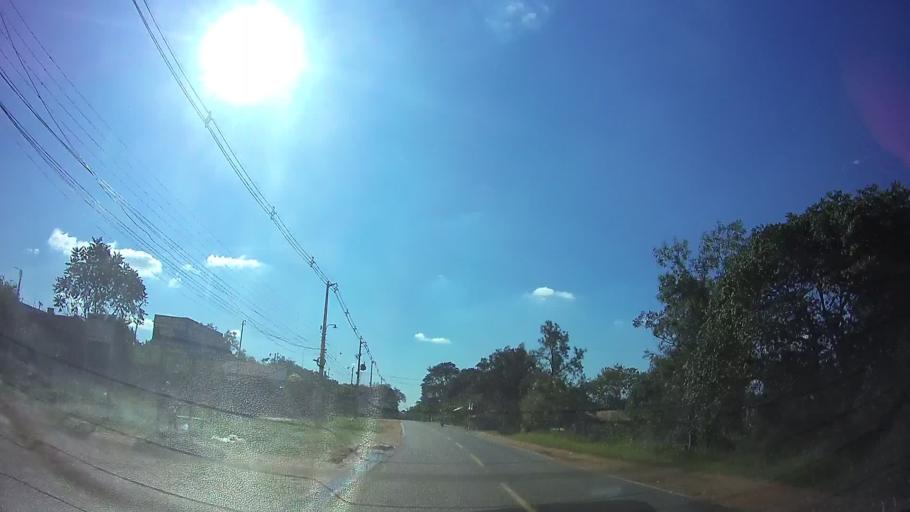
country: PY
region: Central
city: Limpio
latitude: -25.2231
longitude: -57.4778
